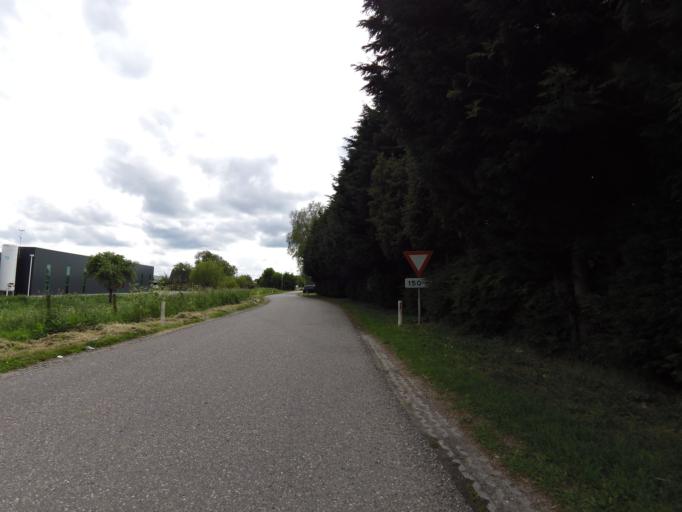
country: NL
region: South Holland
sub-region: Gemeente Brielle
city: Brielle
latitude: 51.8807
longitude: 4.1622
